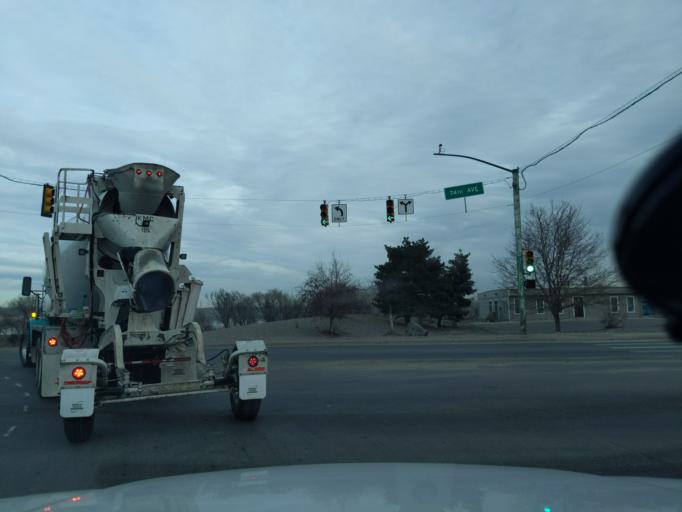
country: US
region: Colorado
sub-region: Adams County
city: Derby
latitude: 39.8307
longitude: -104.9382
